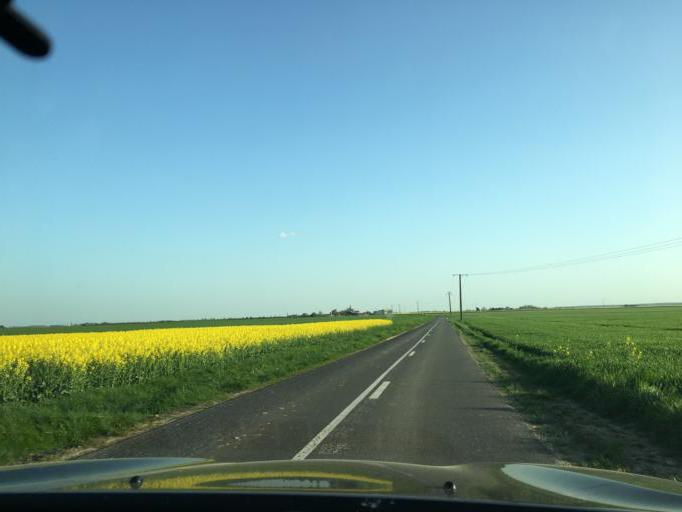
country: FR
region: Centre
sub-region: Departement du Loir-et-Cher
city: Ouzouer-le-Marche
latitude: 47.9032
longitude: 1.5285
